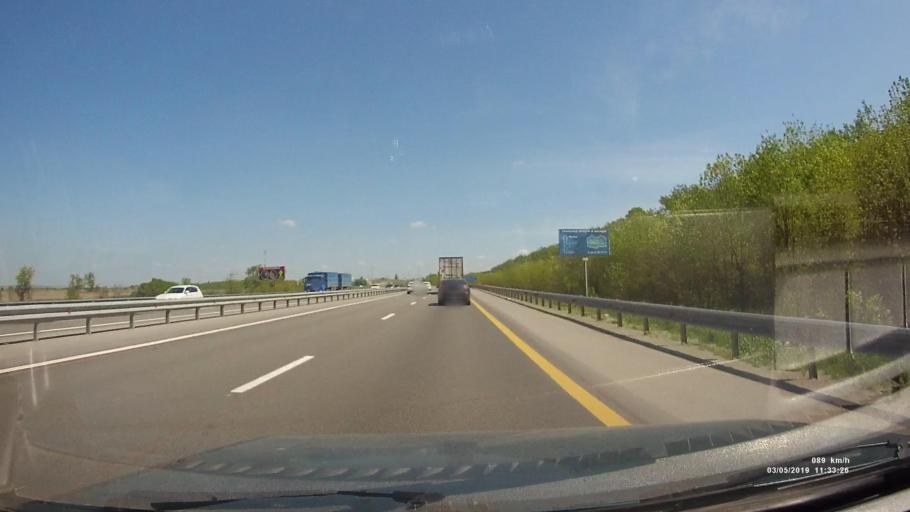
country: RU
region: Rostov
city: Ol'ginskaya
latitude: 47.1240
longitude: 39.8700
